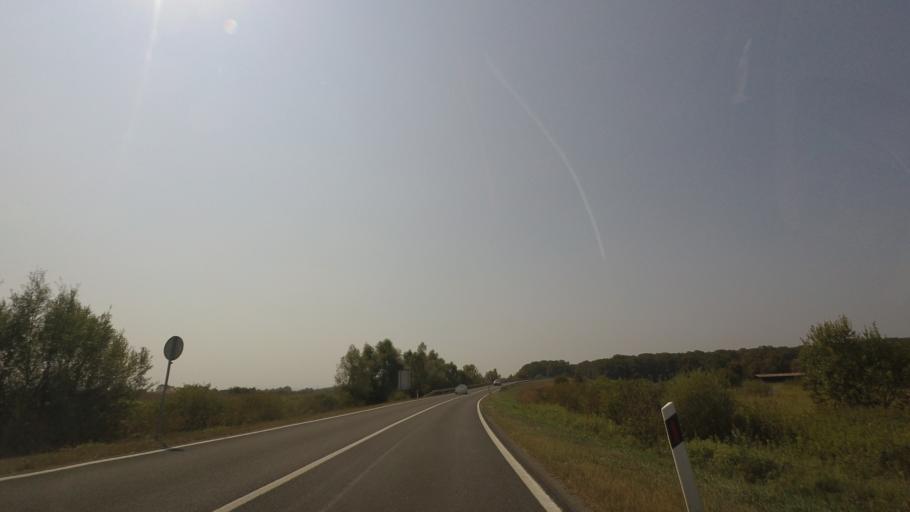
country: HR
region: Sisacko-Moslavacka
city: Novska
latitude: 45.3381
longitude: 16.9559
